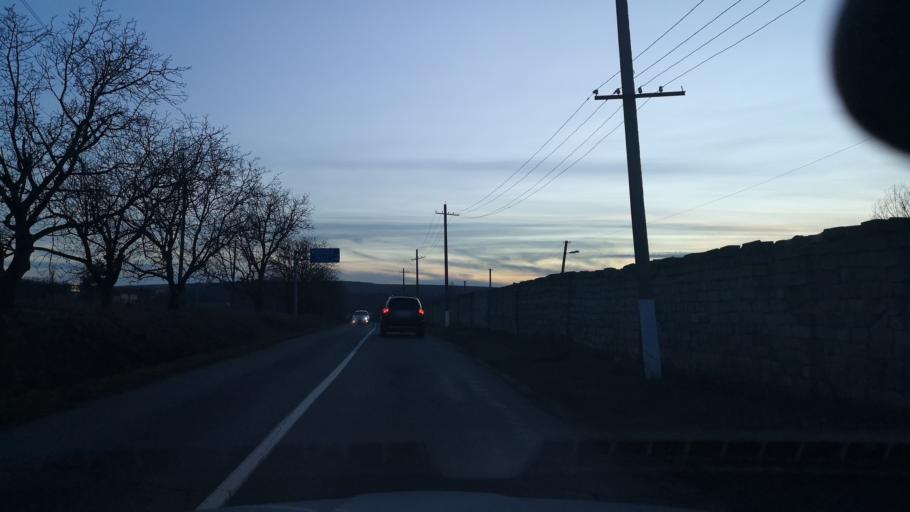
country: MD
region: Orhei
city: Orhei
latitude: 47.3091
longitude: 28.9385
